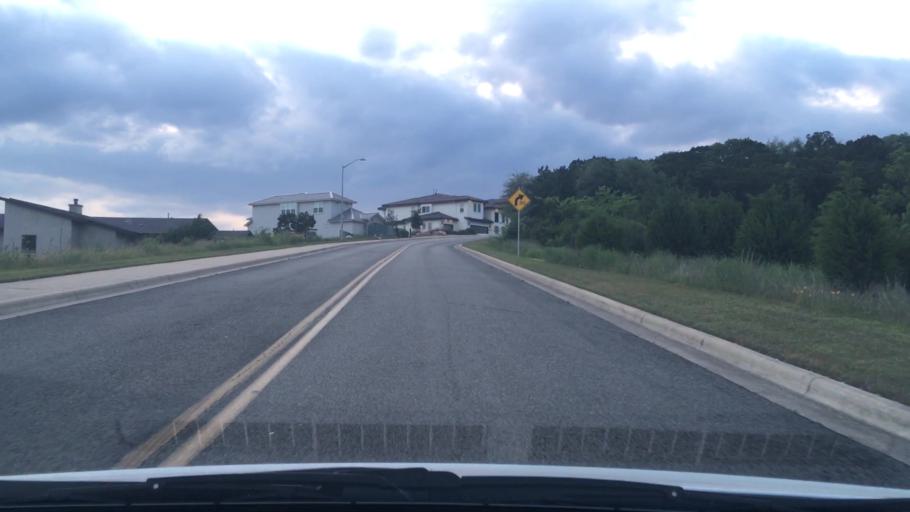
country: US
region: Texas
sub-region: Williamson County
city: Anderson Mill
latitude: 30.4513
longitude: -97.8572
